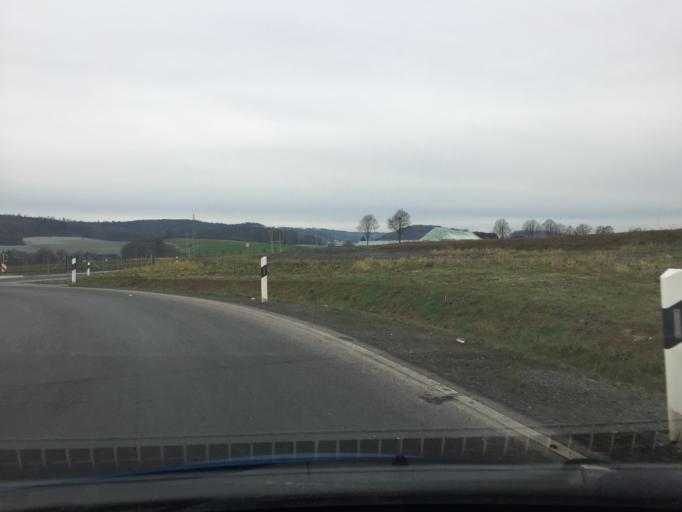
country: DE
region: Lower Saxony
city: Luerdissen
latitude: 51.9441
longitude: 9.6295
